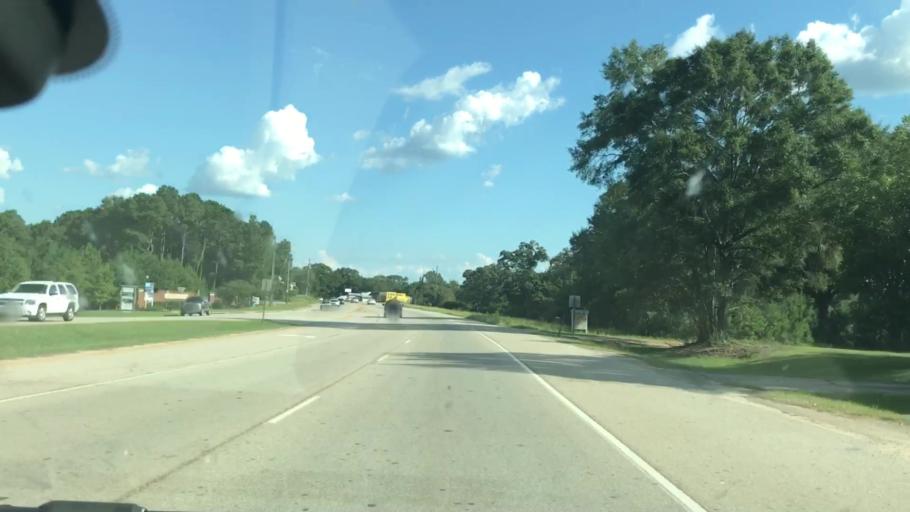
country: US
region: Georgia
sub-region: Troup County
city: La Grange
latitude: 32.9965
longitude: -85.0097
